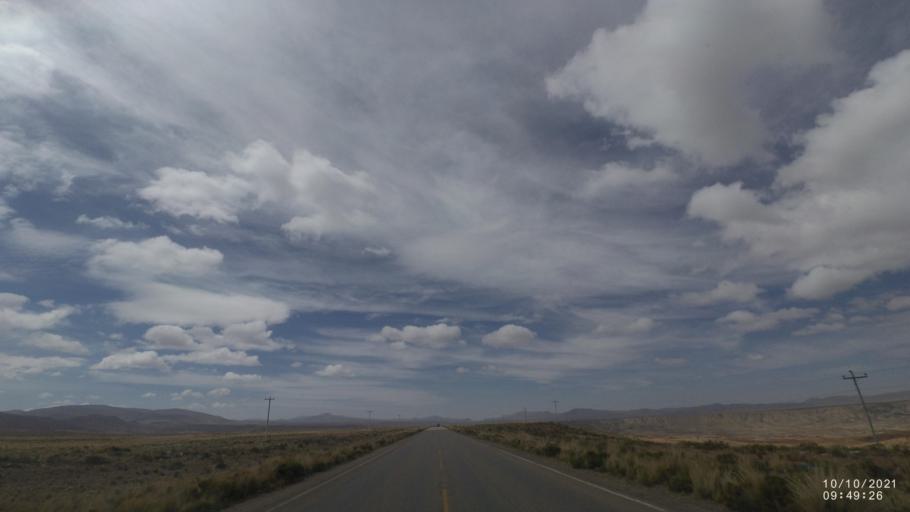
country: BO
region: La Paz
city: Colquiri
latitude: -17.2265
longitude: -67.3381
